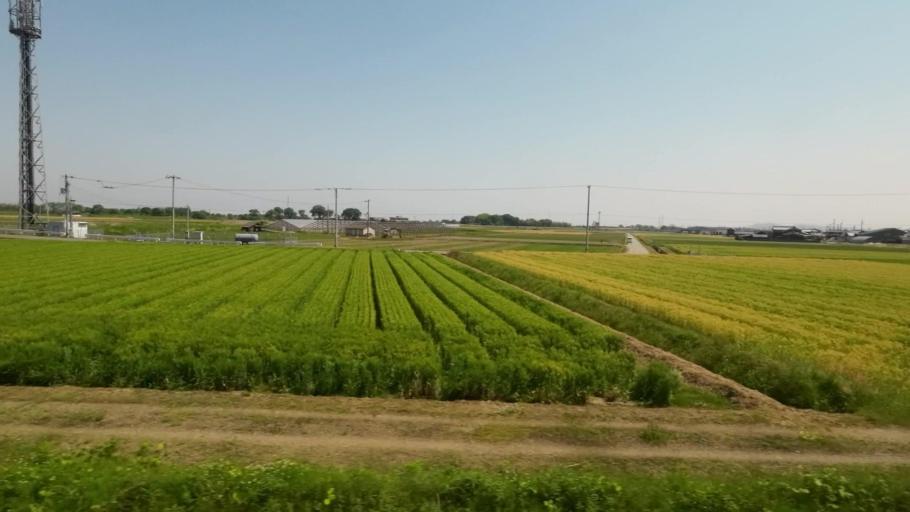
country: JP
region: Ehime
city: Saijo
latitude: 33.8995
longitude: 133.1019
